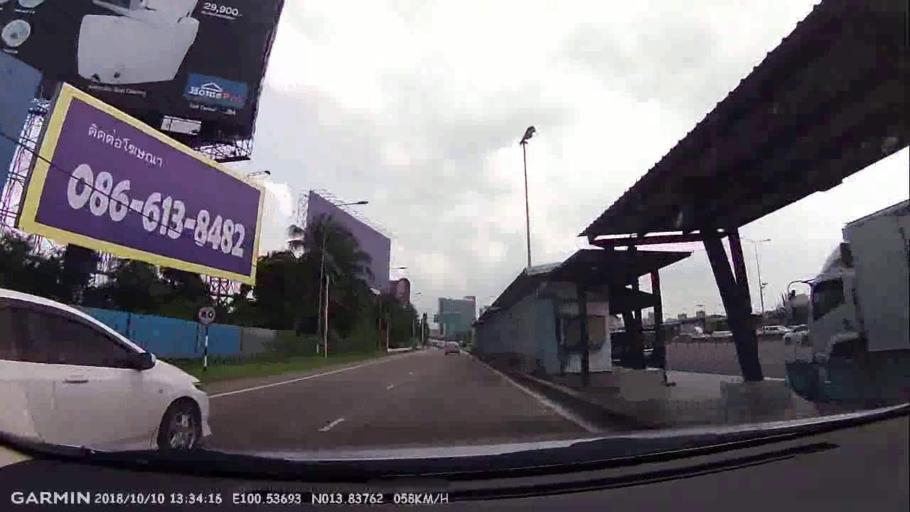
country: TH
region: Bangkok
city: Chatuchak
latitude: 13.8376
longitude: 100.5370
